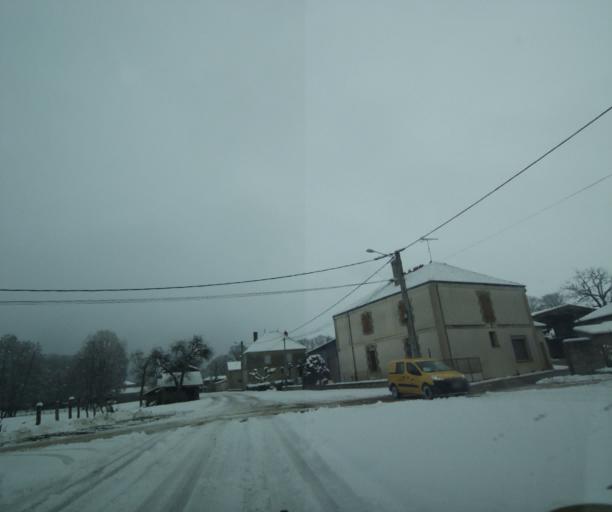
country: FR
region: Champagne-Ardenne
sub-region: Departement de la Haute-Marne
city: Montier-en-Der
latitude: 48.5365
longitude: 4.8115
